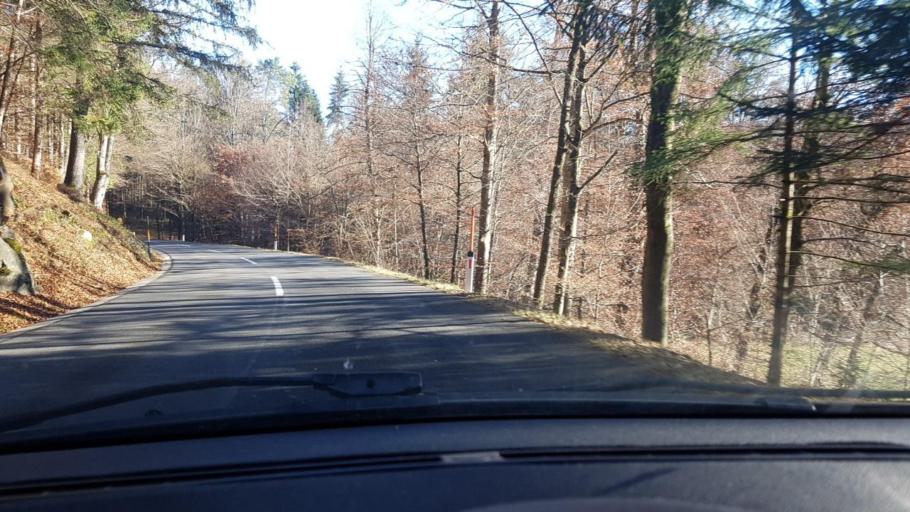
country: AT
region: Carinthia
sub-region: Politischer Bezirk Klagenfurt Land
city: Maria Worth
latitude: 46.5930
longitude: 14.1586
